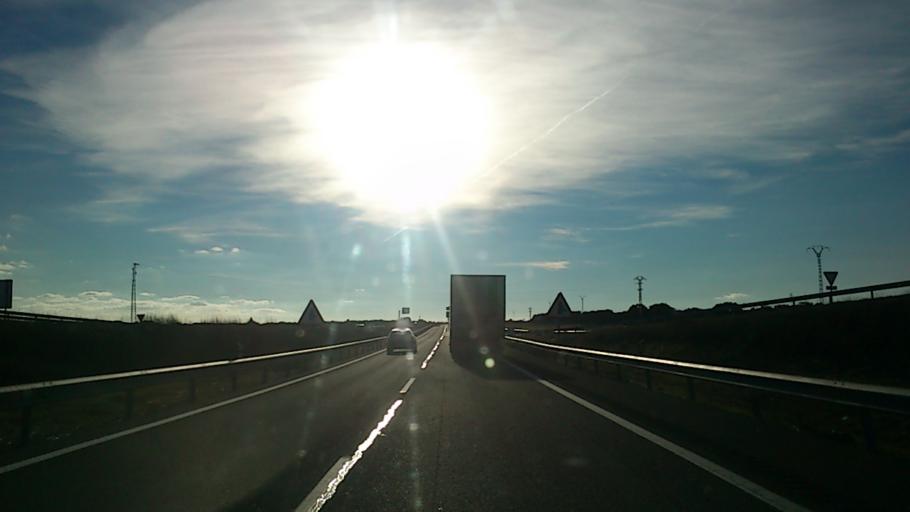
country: ES
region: Castille-La Mancha
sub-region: Provincia de Guadalajara
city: Mirabueno
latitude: 40.9297
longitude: -2.7147
